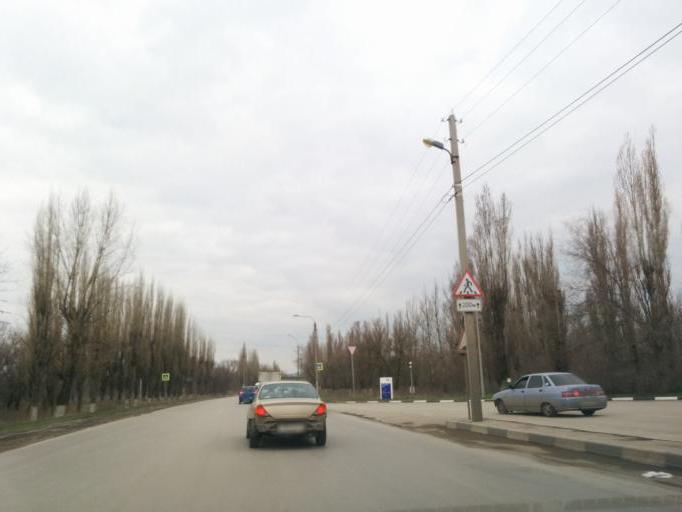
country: RU
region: Rostov
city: Novocherkassk
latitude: 47.4810
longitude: 40.1030
